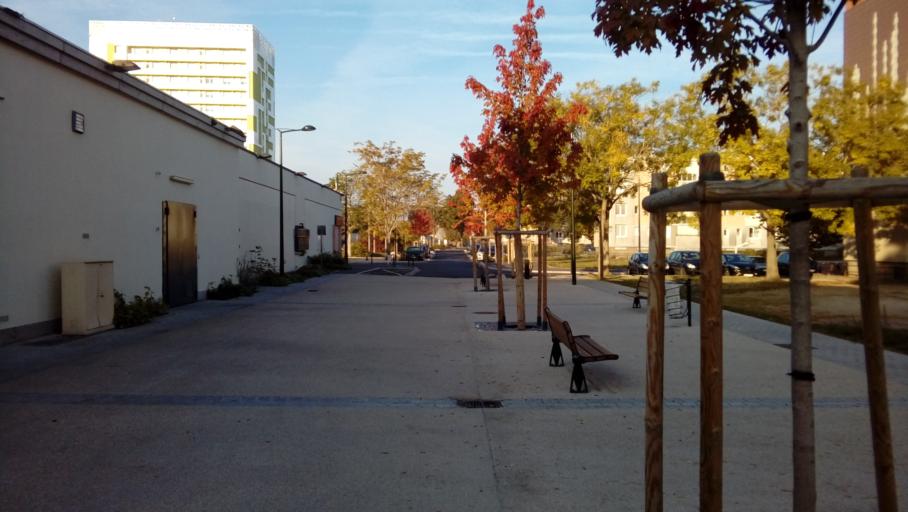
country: FR
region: Centre
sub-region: Departement du Loiret
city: Saint-Jean-le-Blanc
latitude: 47.9123
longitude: 1.9288
